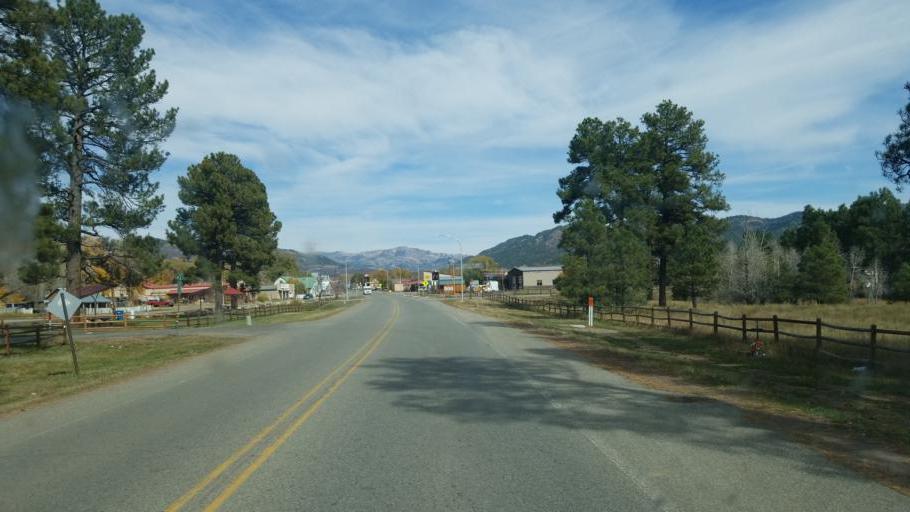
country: US
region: New Mexico
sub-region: Rio Arriba County
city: Chama
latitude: 36.8994
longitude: -106.5811
